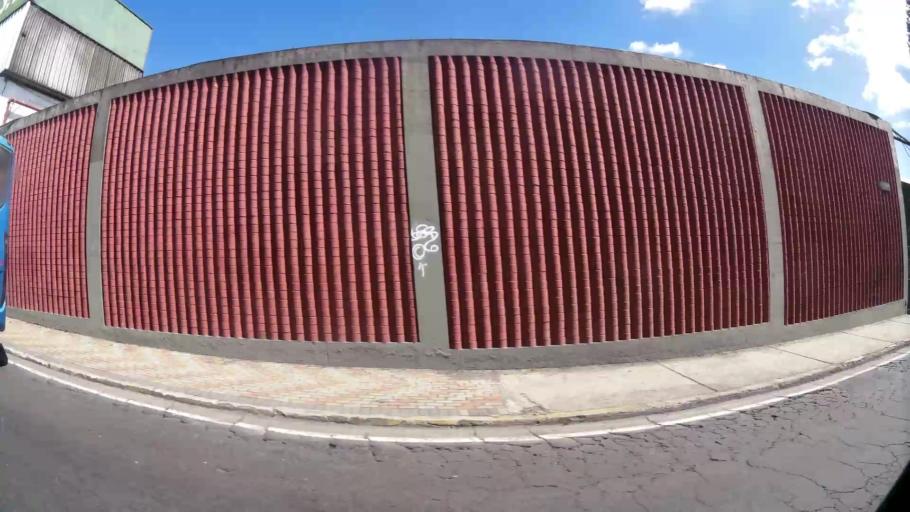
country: EC
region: Pichincha
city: Quito
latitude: -0.2950
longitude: -78.5405
